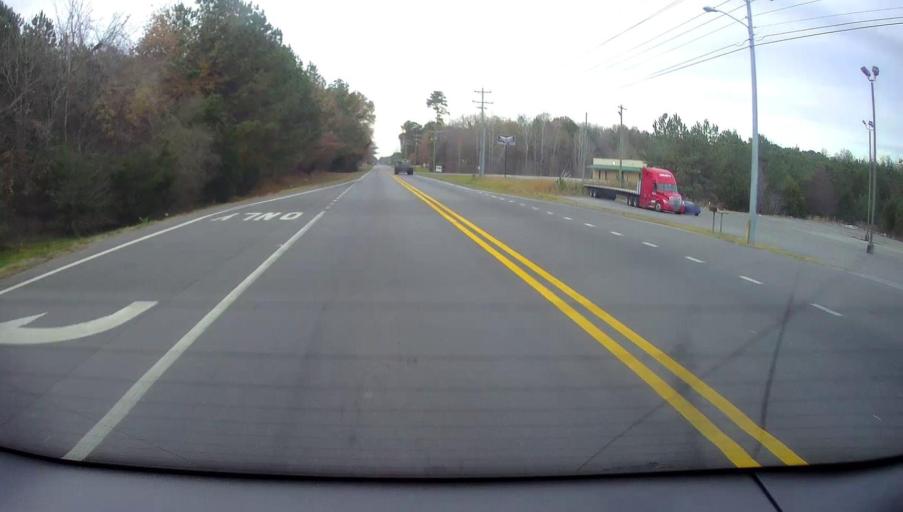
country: US
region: Alabama
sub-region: Morgan County
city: Priceville
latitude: 34.4473
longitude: -86.7582
